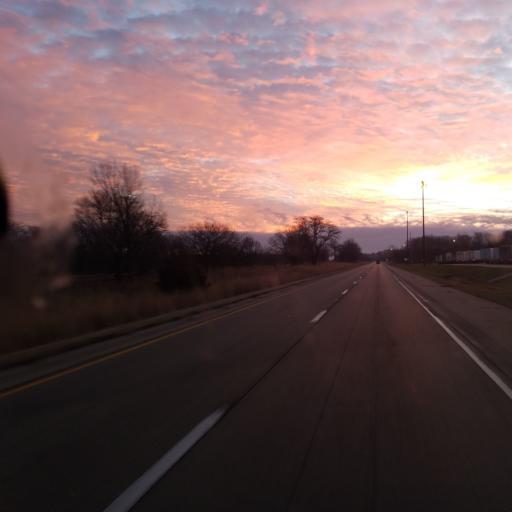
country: US
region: Illinois
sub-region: McLean County
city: Danvers
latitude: 40.6133
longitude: -89.2469
